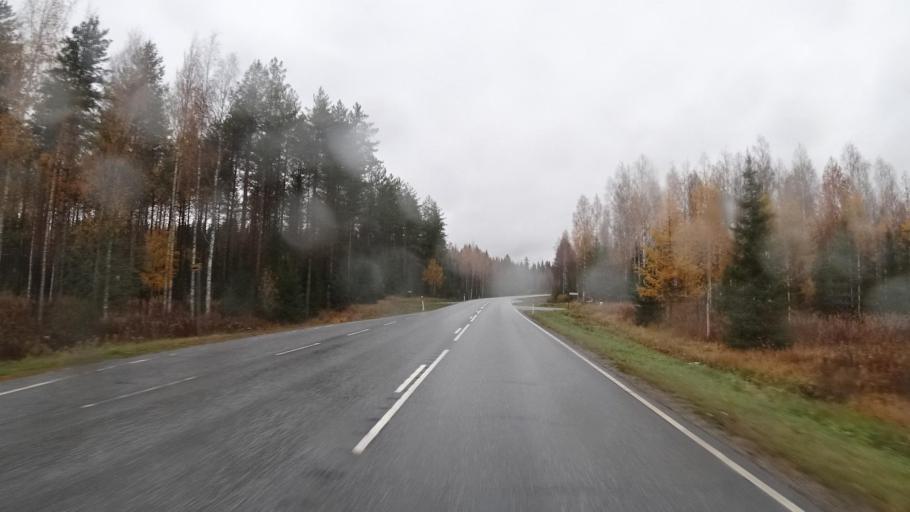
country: FI
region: Northern Savo
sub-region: Varkaus
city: Kangaslampi
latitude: 62.4726
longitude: 28.3251
